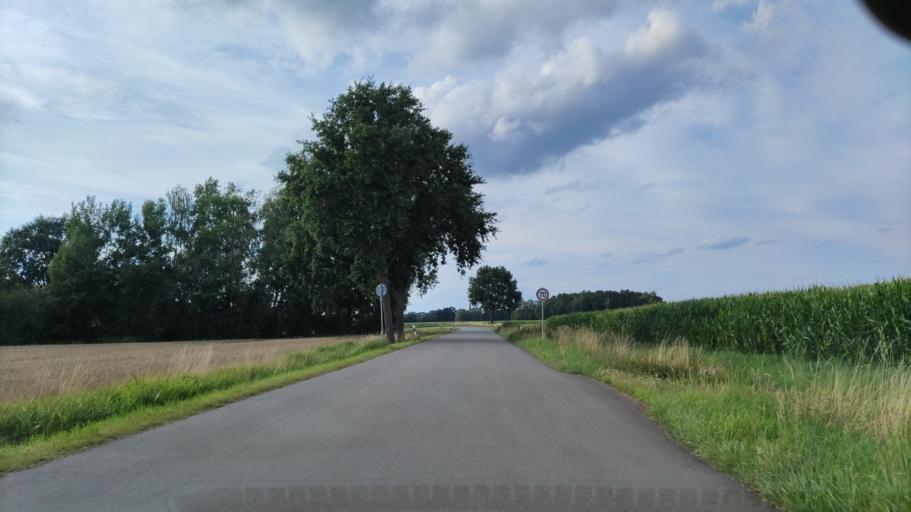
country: DE
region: Lower Saxony
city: Dannenberg
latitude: 53.0859
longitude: 11.1024
